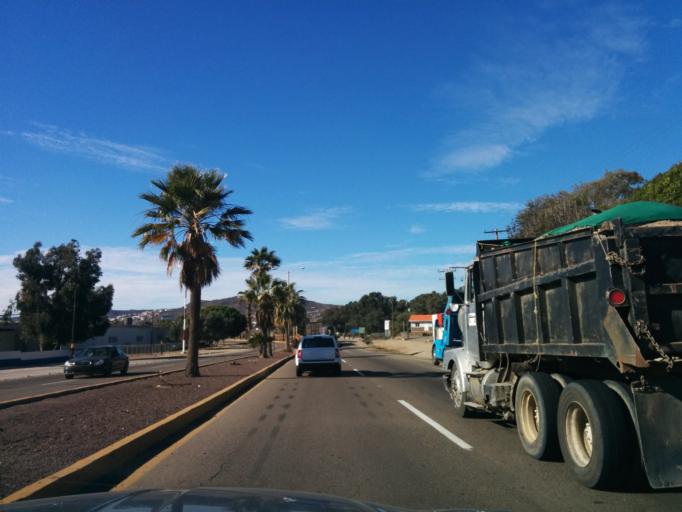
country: MX
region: Baja California
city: El Sauzal
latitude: 31.8965
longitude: -116.6997
